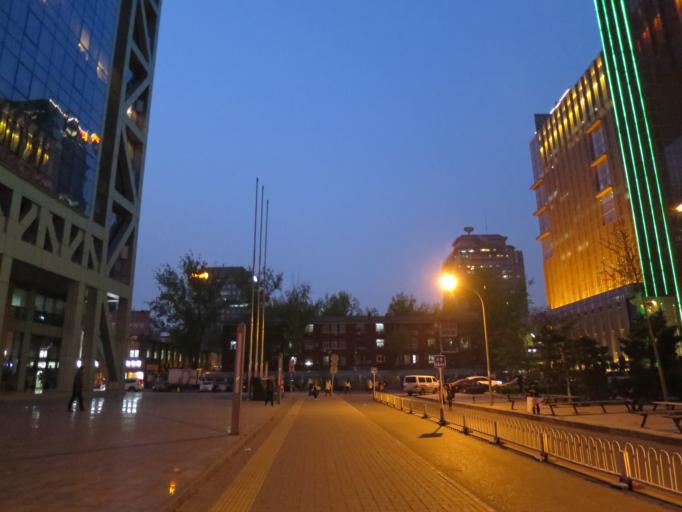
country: CN
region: Beijing
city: Chaowai
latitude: 39.9038
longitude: 116.4448
